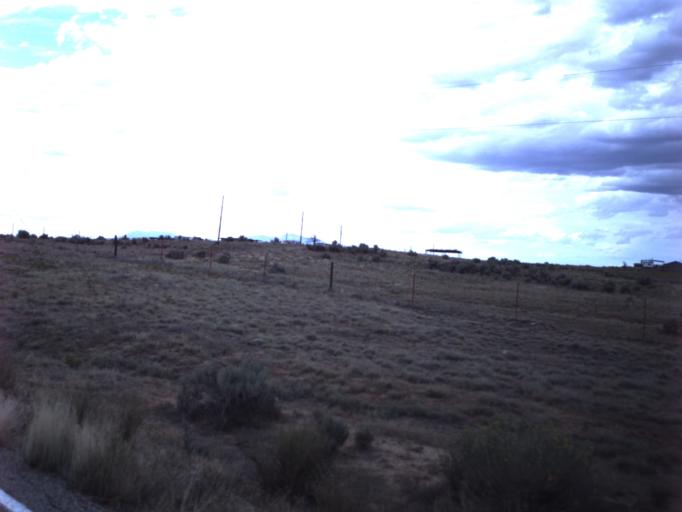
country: US
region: Utah
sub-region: San Juan County
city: Blanding
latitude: 37.4210
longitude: -109.3354
